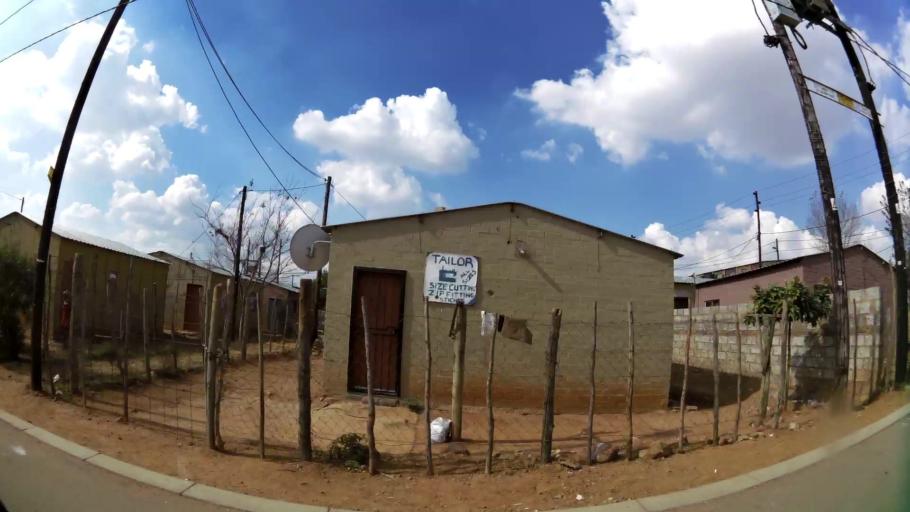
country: ZA
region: Gauteng
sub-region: City of Johannesburg Metropolitan Municipality
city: Roodepoort
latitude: -26.1836
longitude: 27.8459
